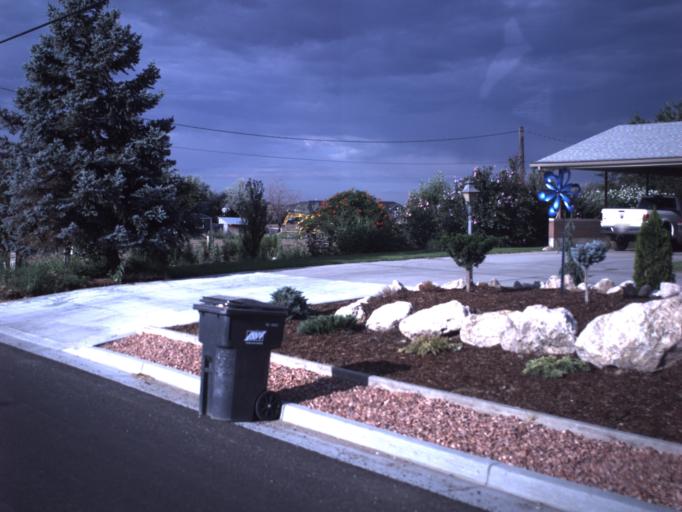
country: US
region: Utah
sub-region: Weber County
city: West Haven
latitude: 41.2011
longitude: -112.0932
